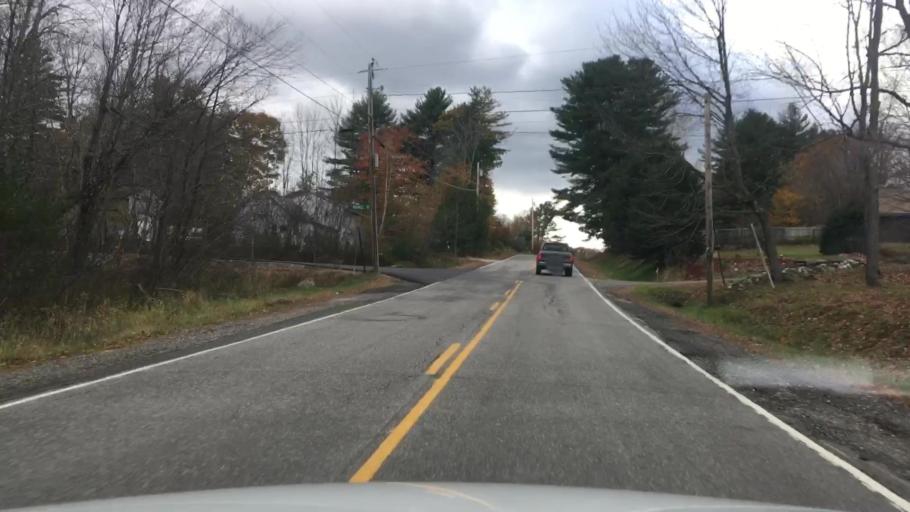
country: US
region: Maine
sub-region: Androscoggin County
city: Sabattus
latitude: 44.1351
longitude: -70.0193
